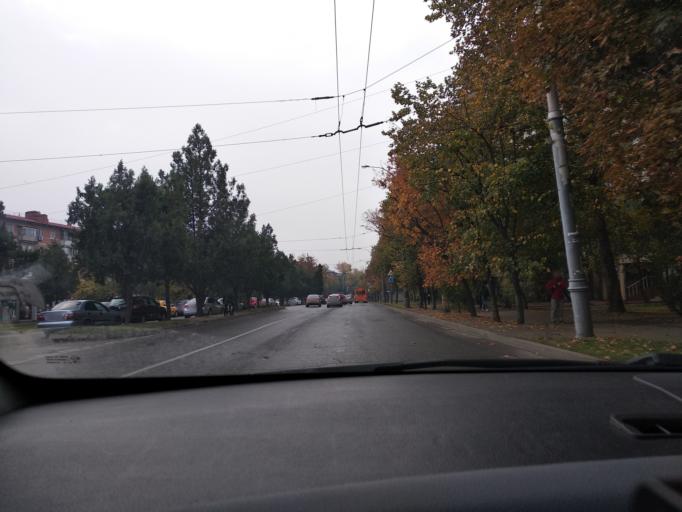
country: RU
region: Krasnodarskiy
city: Krasnodar
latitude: 45.0583
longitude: 38.9609
